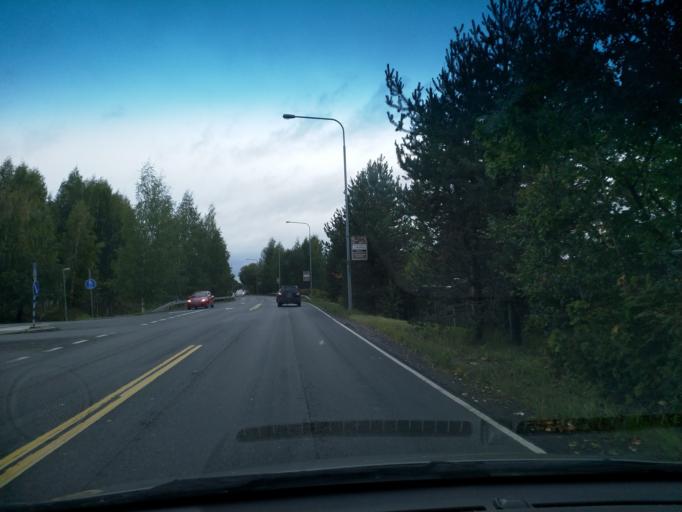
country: FI
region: Pirkanmaa
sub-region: Tampere
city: Tampere
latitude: 61.4788
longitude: 23.8384
